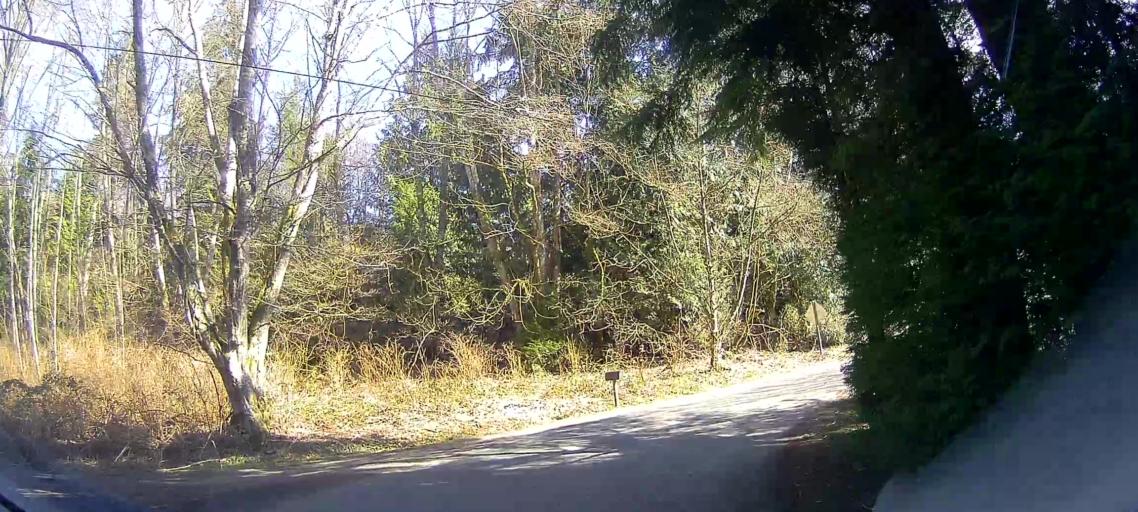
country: US
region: Washington
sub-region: Skagit County
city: Burlington
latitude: 48.5930
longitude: -122.3758
